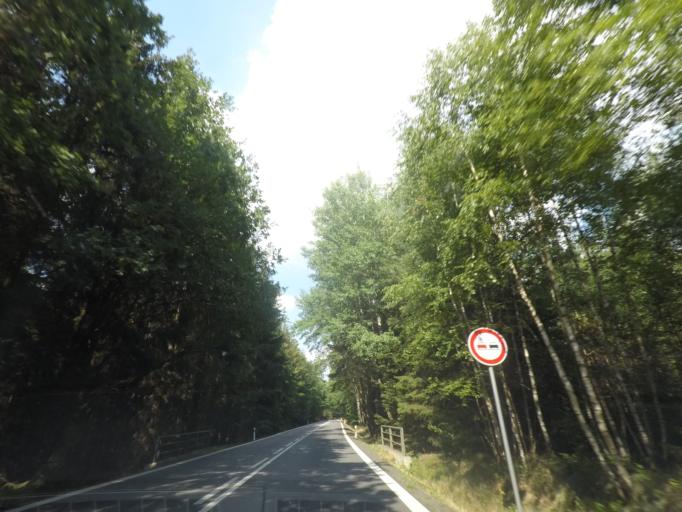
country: CZ
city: Borohradek
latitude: 50.0843
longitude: 16.0771
